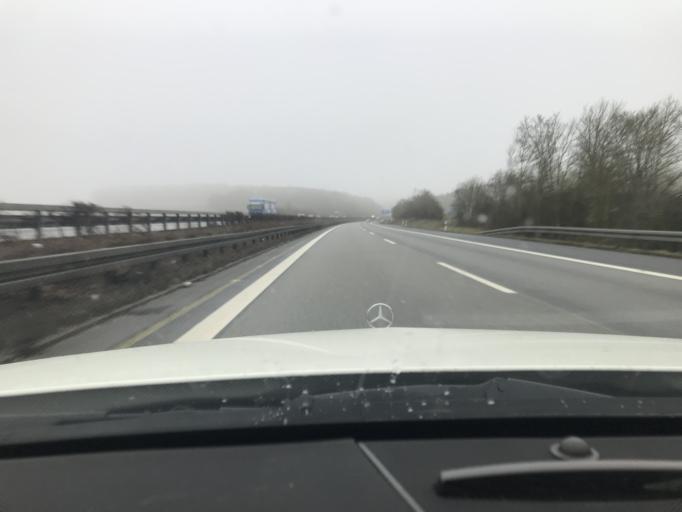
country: DE
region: Bavaria
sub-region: Regierungsbezirk Unterfranken
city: Werneck
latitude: 50.0274
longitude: 10.0702
